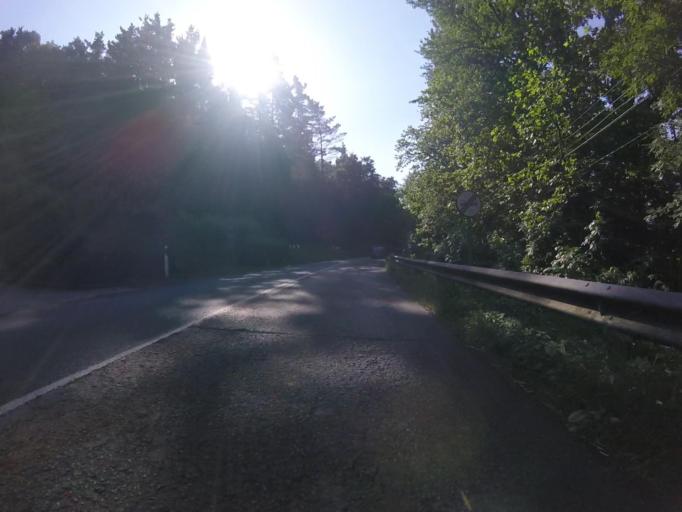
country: ES
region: Basque Country
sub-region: Provincia de Guipuzcoa
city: Asteasu
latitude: 43.1919
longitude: -2.0912
